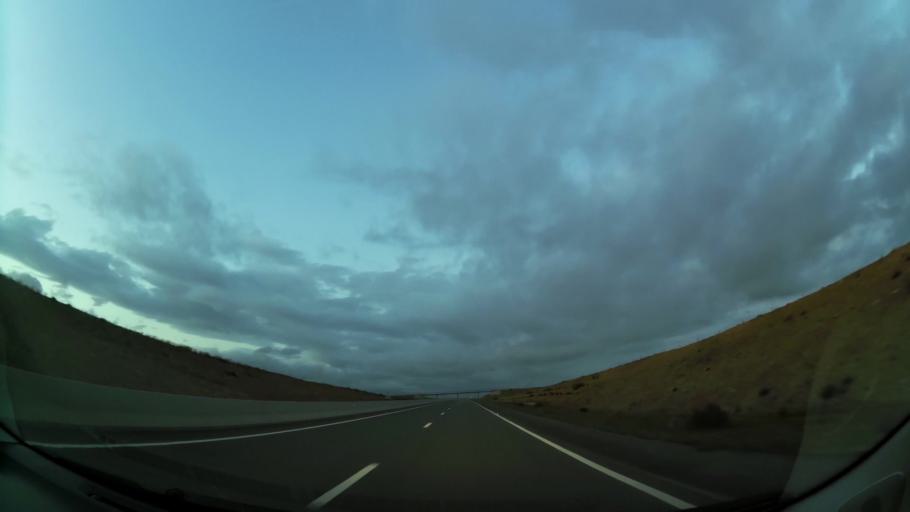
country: MA
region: Oriental
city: El Aioun
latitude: 34.6204
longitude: -2.4018
